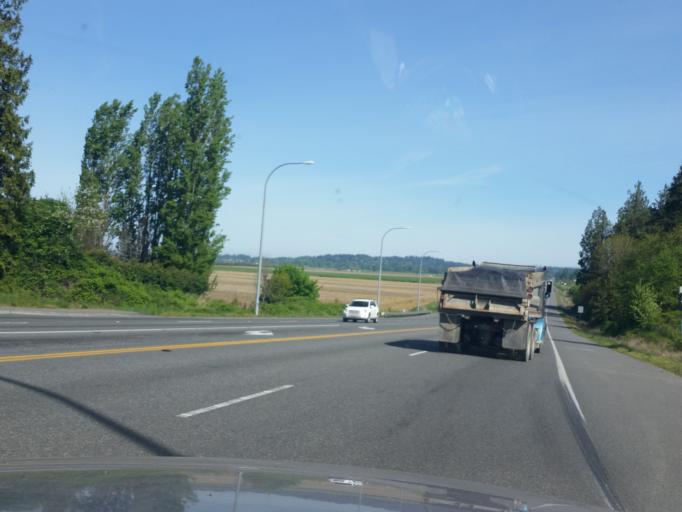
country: US
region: Washington
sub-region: Snohomish County
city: Cathcart
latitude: 47.8782
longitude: -122.1097
